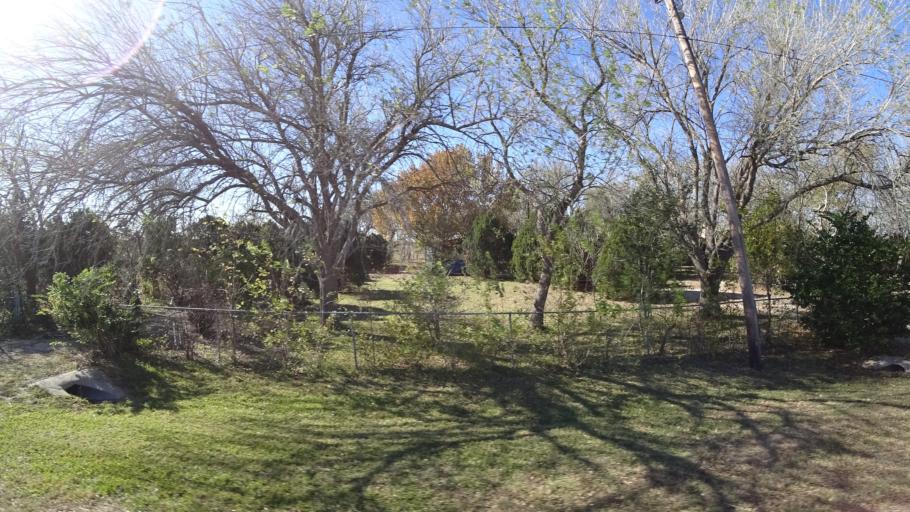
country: US
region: Texas
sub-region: Travis County
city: Onion Creek
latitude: 30.0970
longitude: -97.6624
